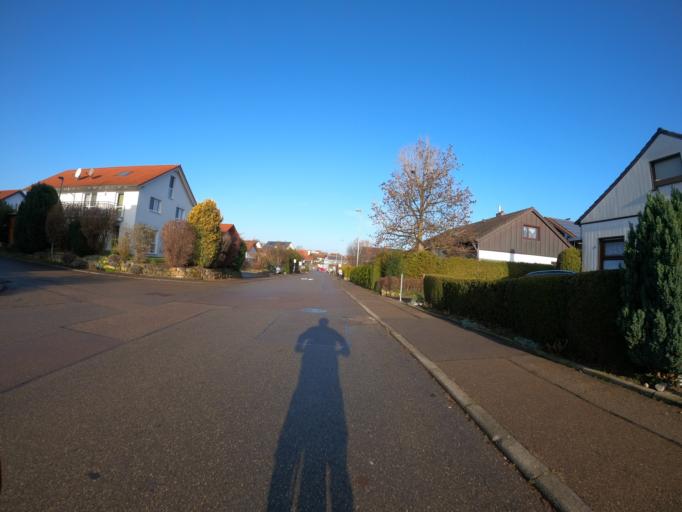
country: DE
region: Baden-Wuerttemberg
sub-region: Regierungsbezirk Stuttgart
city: Hattenhofen
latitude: 48.6651
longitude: 9.5763
